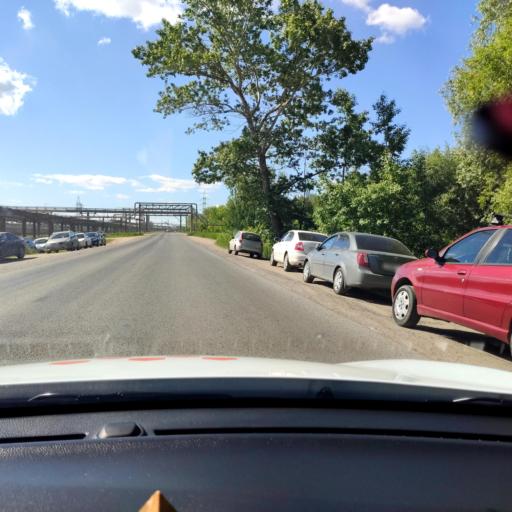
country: RU
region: Tatarstan
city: Staroye Arakchino
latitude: 55.8815
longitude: 48.9761
